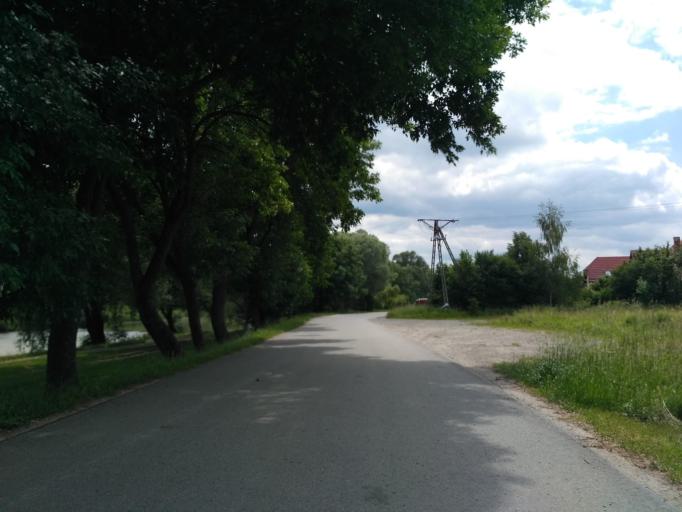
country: PL
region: Subcarpathian Voivodeship
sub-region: Powiat rzeszowski
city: Dynow
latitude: 49.8069
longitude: 22.2427
